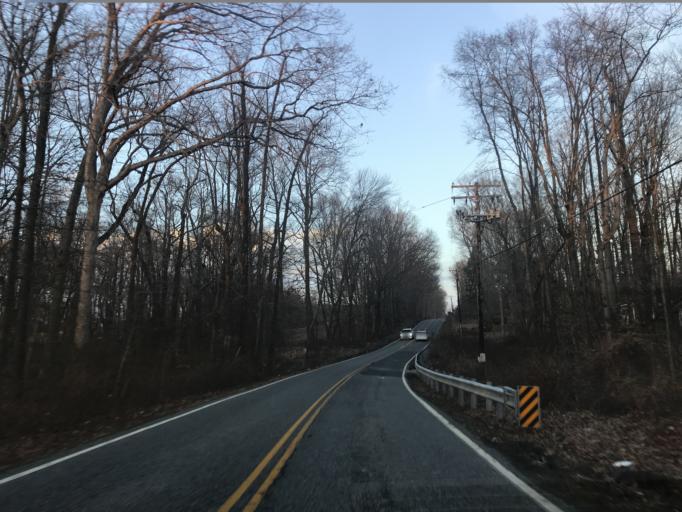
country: US
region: Maryland
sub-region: Harford County
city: Bel Air South
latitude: 39.5254
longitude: -76.2856
